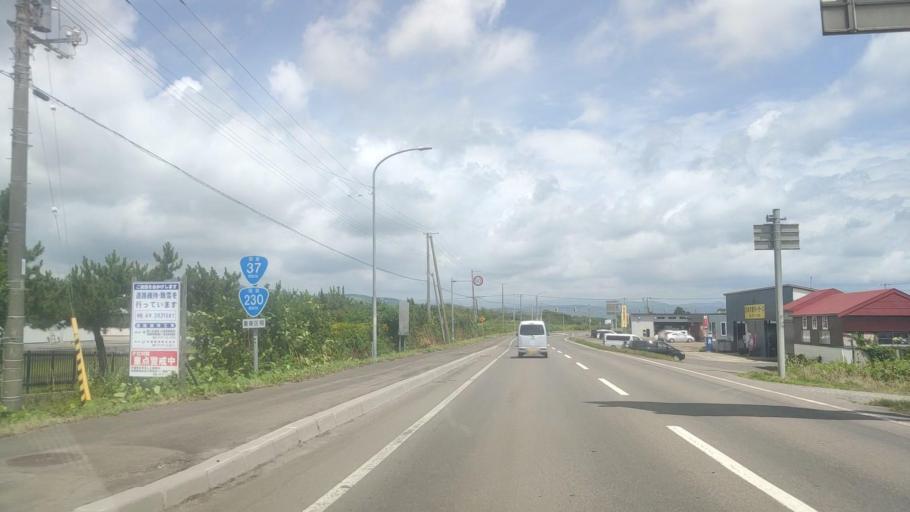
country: JP
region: Hokkaido
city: Niseko Town
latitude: 42.5199
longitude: 140.3828
